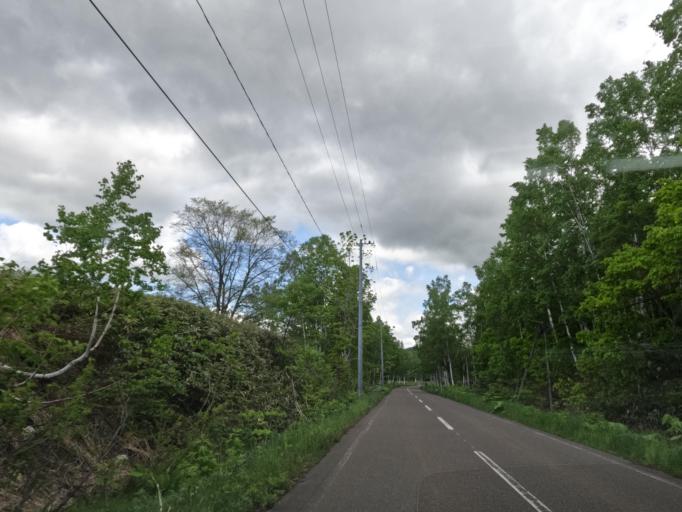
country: JP
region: Hokkaido
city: Tobetsu
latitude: 43.4559
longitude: 141.5916
